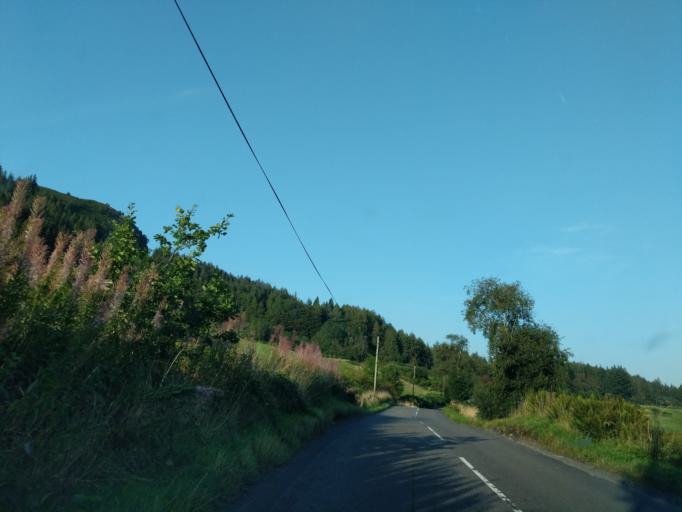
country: GB
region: Scotland
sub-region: Stirling
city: Balfron
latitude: 56.1745
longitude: -4.3588
